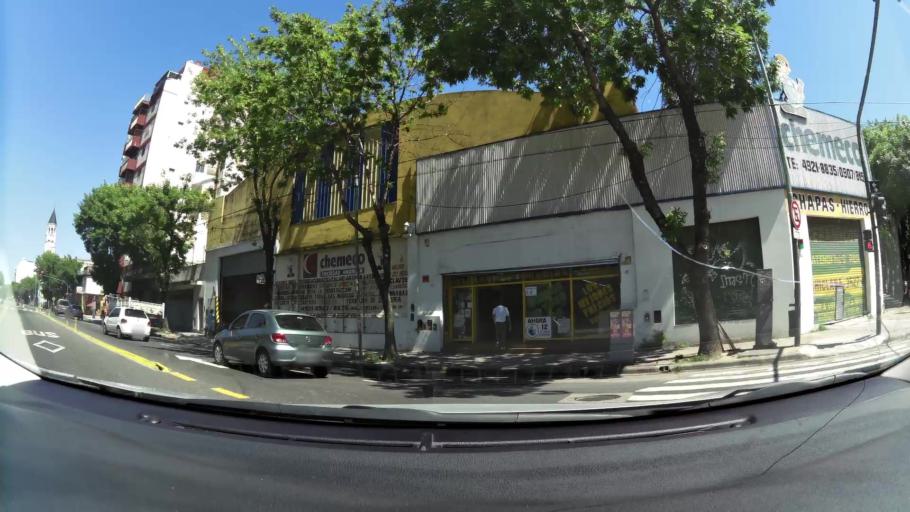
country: AR
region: Buenos Aires F.D.
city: Buenos Aires
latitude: -34.6361
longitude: -58.4139
